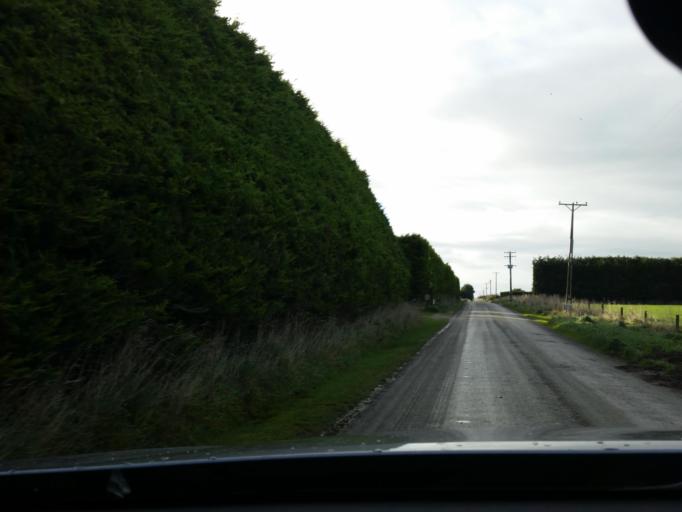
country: NZ
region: Southland
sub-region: Invercargill City
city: Invercargill
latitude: -46.3309
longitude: 168.4230
